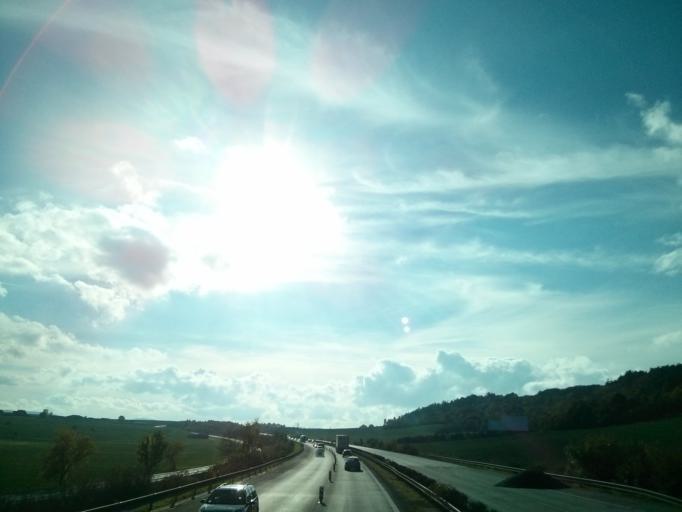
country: CZ
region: Central Bohemia
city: Zebrak
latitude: 49.8865
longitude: 13.9200
